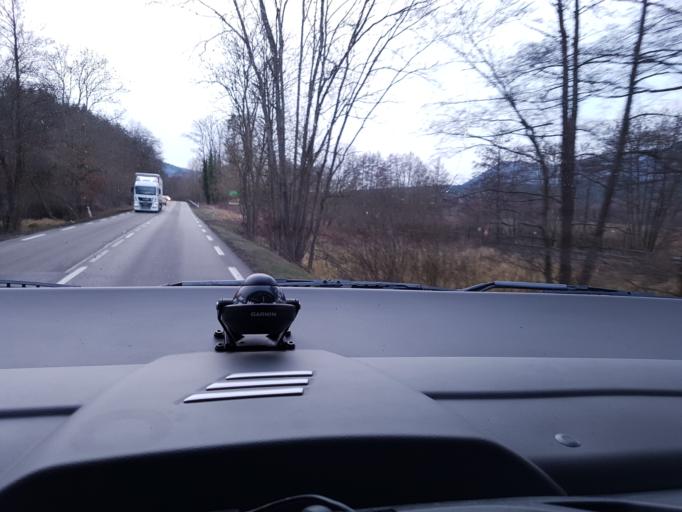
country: FR
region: Alsace
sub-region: Departement du Bas-Rhin
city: Chatenois
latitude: 48.2804
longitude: 7.3564
